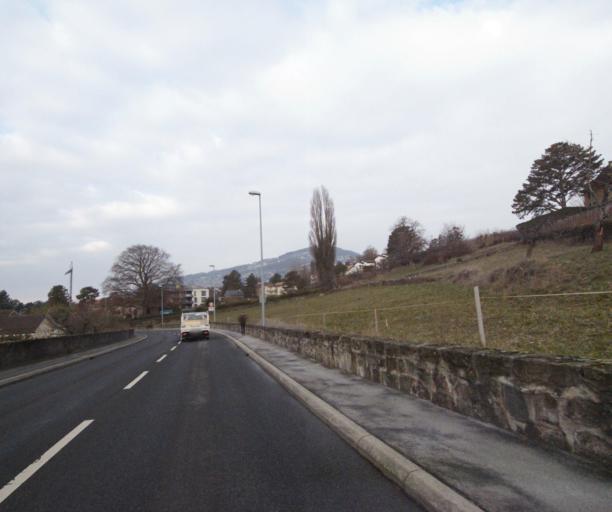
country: CH
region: Vaud
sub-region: Riviera-Pays-d'Enhaut District
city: La Tour-de-Peilz
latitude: 46.4616
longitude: 6.8620
